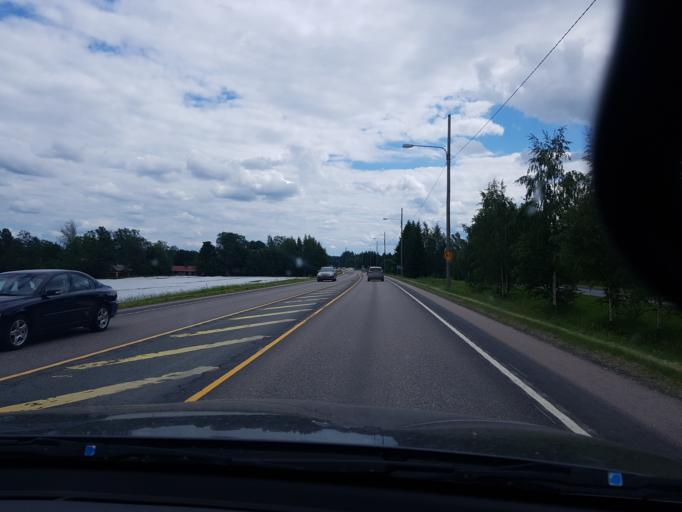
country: FI
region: Pirkanmaa
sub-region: Tampere
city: Paelkaene
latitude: 61.3447
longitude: 24.2627
